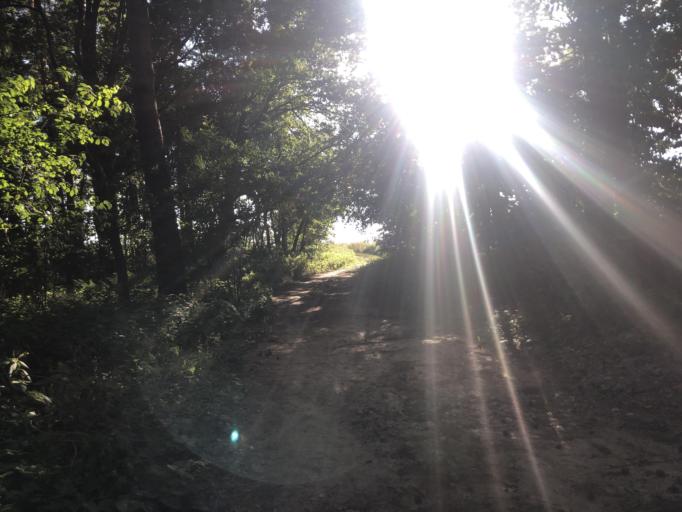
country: DE
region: Lower Saxony
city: Tosterglope
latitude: 53.2579
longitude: 10.7904
